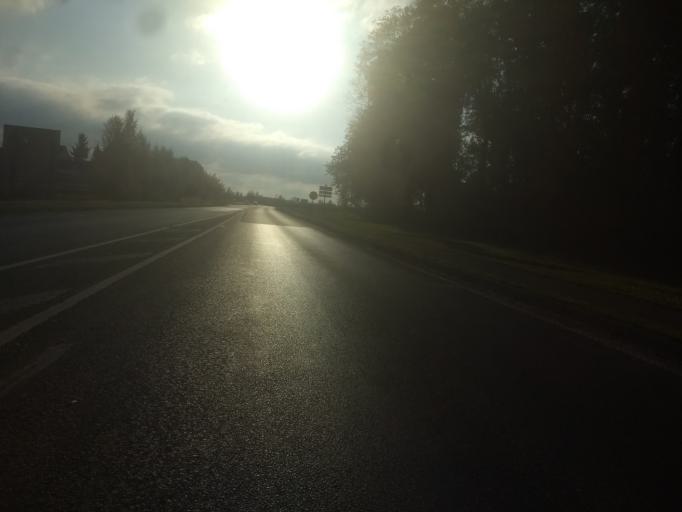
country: FR
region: Nord-Pas-de-Calais
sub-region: Departement du Pas-de-Calais
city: Tilloy-les-Mofflaines
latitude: 50.2785
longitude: 2.8132
